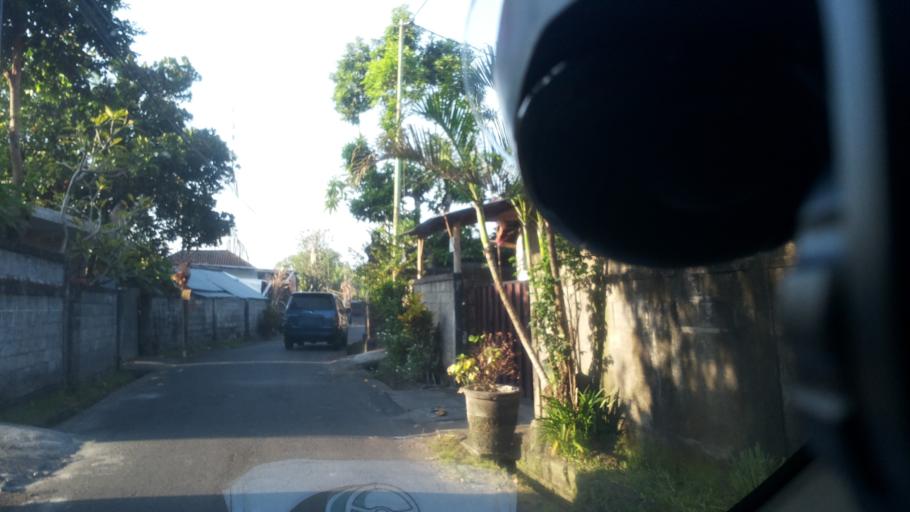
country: ID
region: Bali
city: Dajan Tangluk
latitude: -8.6402
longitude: 115.2396
